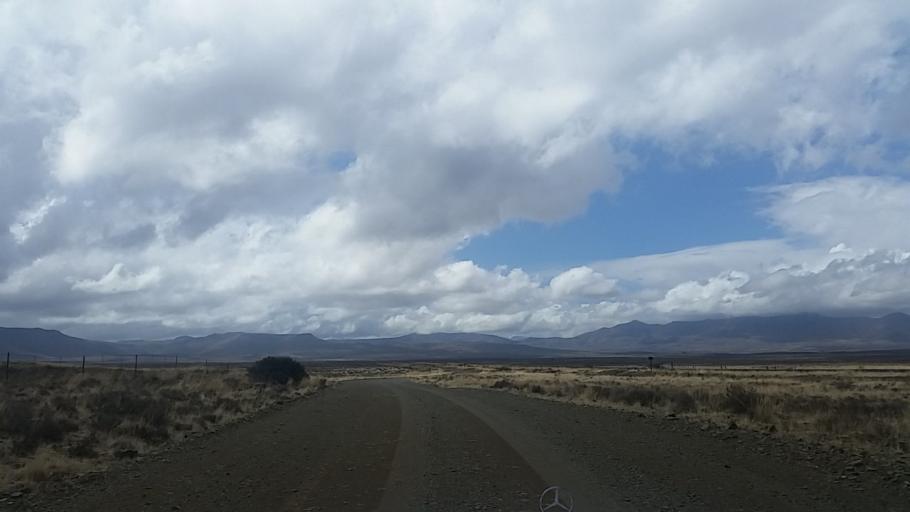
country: ZA
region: Eastern Cape
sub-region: Cacadu District Municipality
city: Graaff-Reinet
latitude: -31.9043
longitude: 24.7582
